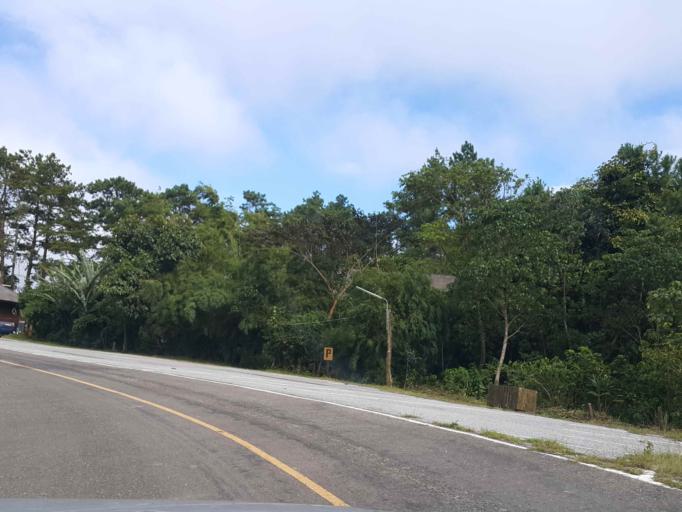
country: TH
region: Tak
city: Tak
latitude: 16.7805
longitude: 98.9280
